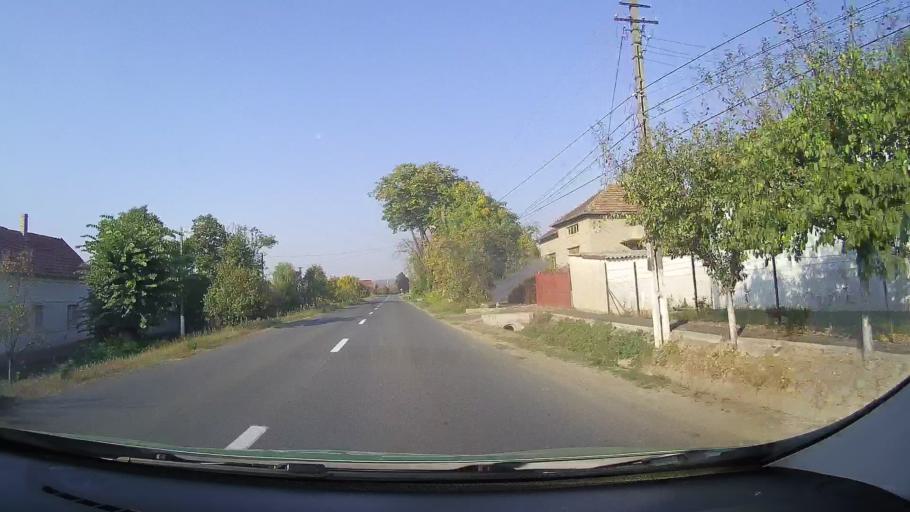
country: RO
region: Arad
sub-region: Comuna Paulis
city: Paulis
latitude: 46.1168
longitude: 21.5964
